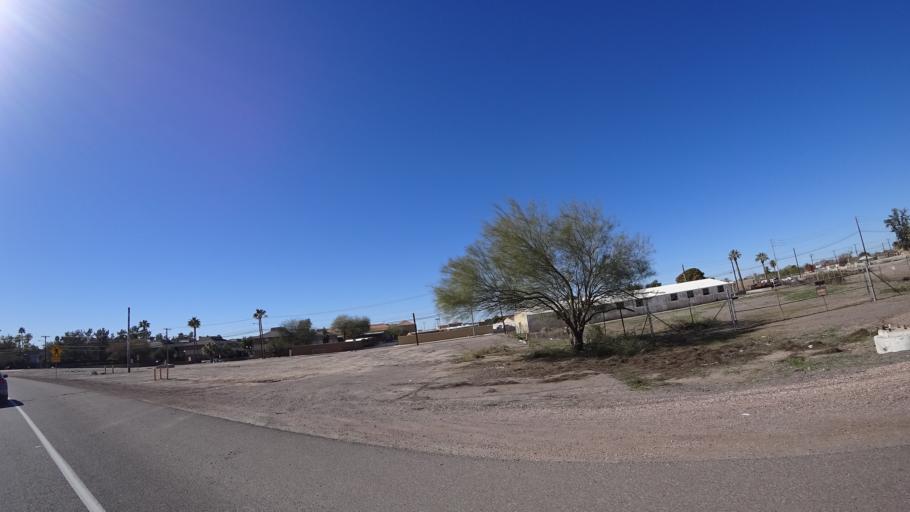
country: US
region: Arizona
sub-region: Maricopa County
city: Buckeye
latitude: 33.3764
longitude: -112.5721
